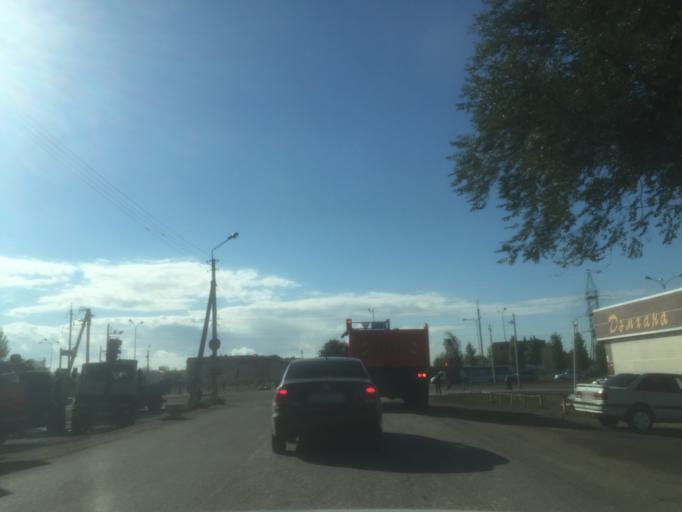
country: KZ
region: Astana Qalasy
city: Astana
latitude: 51.1894
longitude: 71.3455
